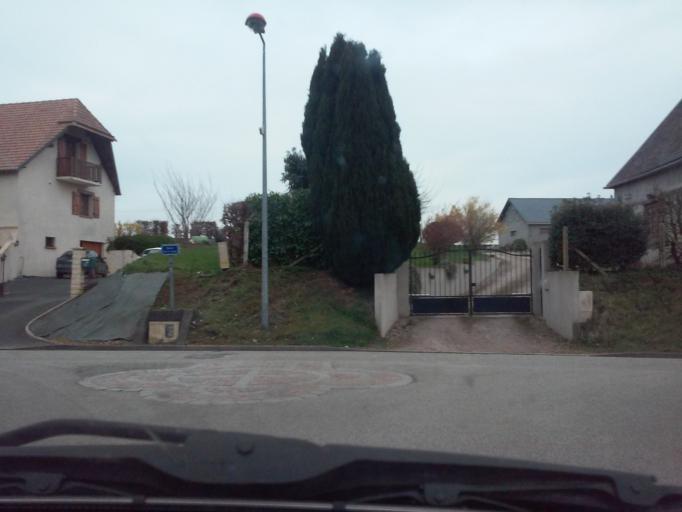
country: FR
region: Haute-Normandie
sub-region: Departement de la Seine-Maritime
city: Lanquetot
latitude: 49.5703
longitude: 0.5377
